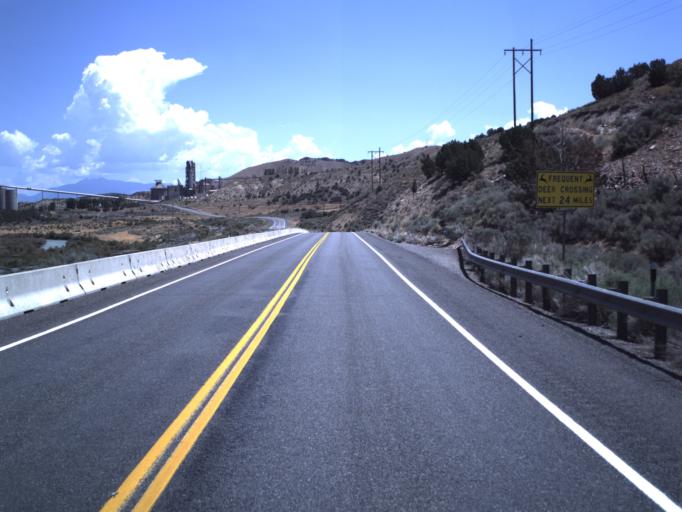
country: US
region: Utah
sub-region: Juab County
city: Nephi
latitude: 39.5559
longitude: -112.2135
